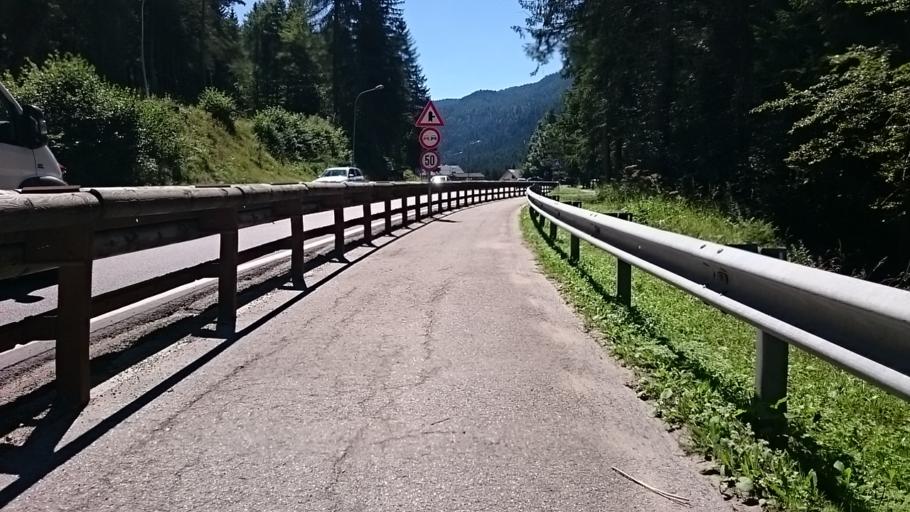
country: IT
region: Veneto
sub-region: Provincia di Belluno
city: Cortina d'Ampezzo
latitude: 46.5094
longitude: 12.1563
